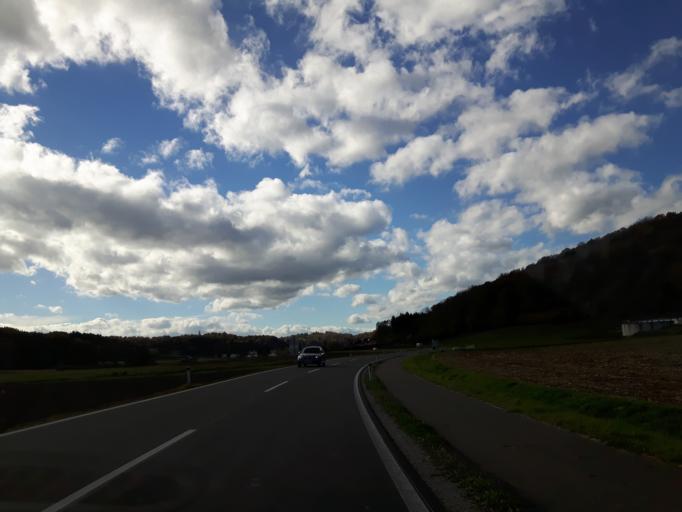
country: AT
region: Styria
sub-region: Politischer Bezirk Suedoststeiermark
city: Paldau
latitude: 46.9488
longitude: 15.8157
